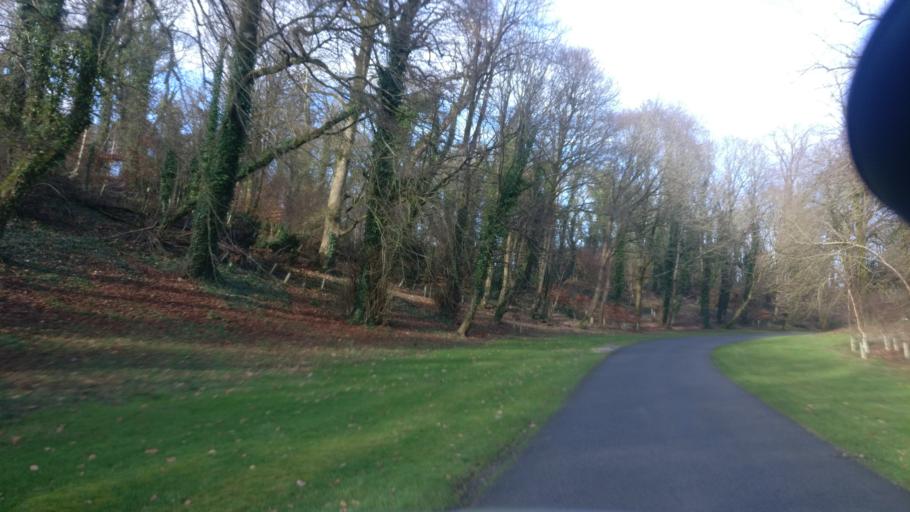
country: IE
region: Leinster
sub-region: Kilkenny
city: Thomastown
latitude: 52.5337
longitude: -7.1819
